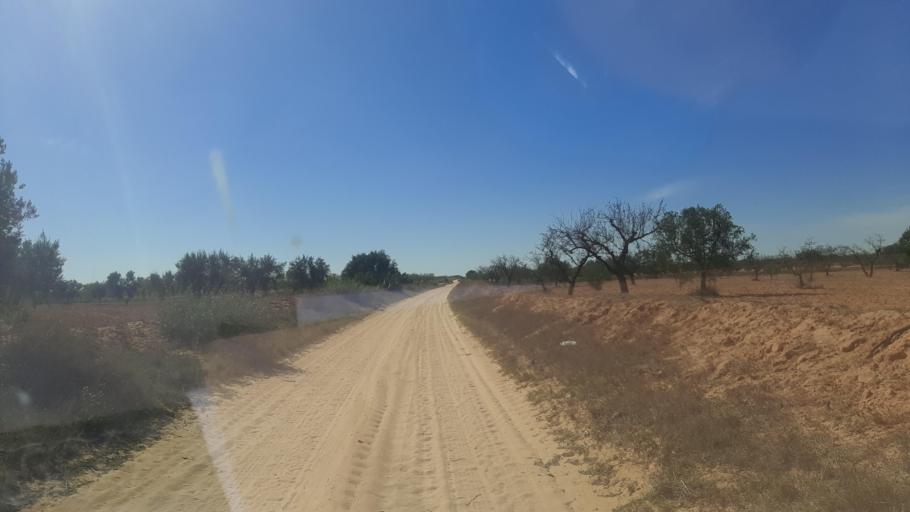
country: TN
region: Safaqis
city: Sfax
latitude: 34.8217
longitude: 10.5523
